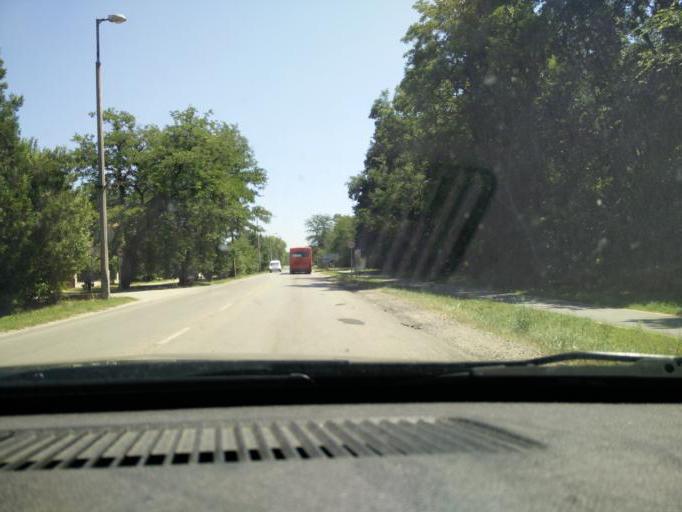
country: HU
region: Komarom-Esztergom
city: Baj
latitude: 47.6408
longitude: 18.3431
